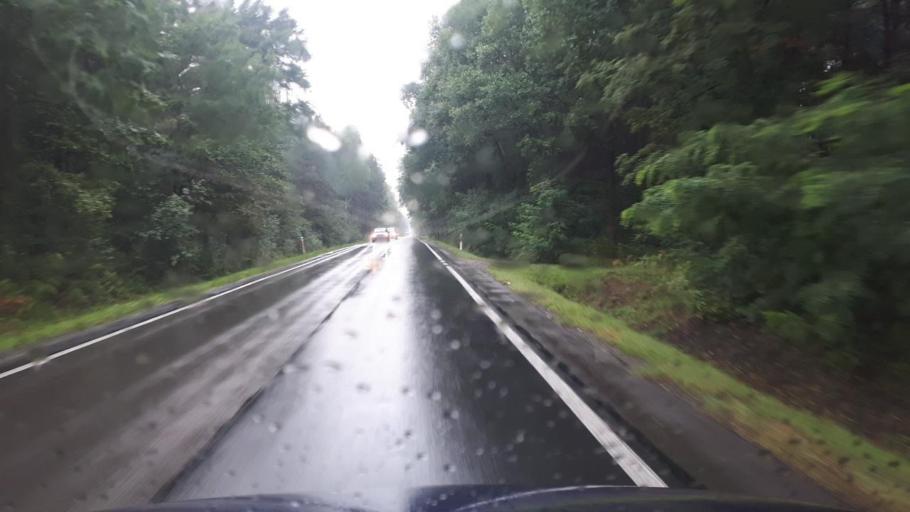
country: PL
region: Silesian Voivodeship
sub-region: Powiat tarnogorski
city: Tworog
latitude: 50.5300
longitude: 18.6838
